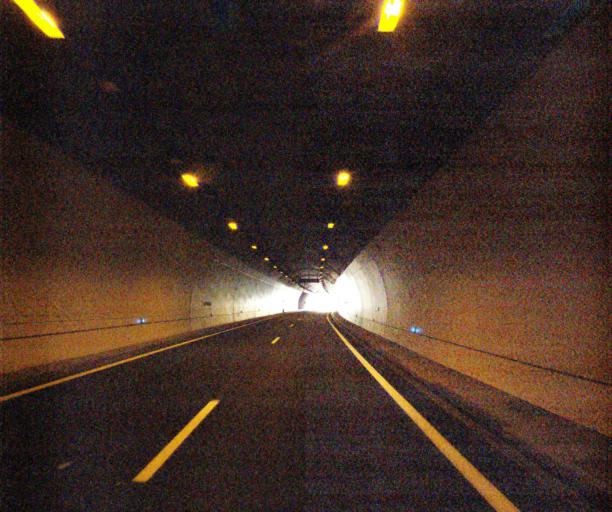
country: FR
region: Rhone-Alpes
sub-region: Departement de l'Isere
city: Vif
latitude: 45.0509
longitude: 5.6857
